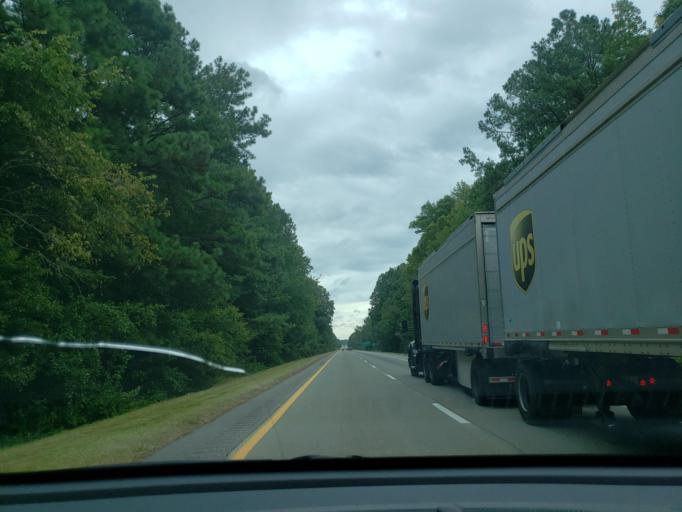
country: US
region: North Carolina
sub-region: Granville County
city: Oxford
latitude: 36.3210
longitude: -78.5117
